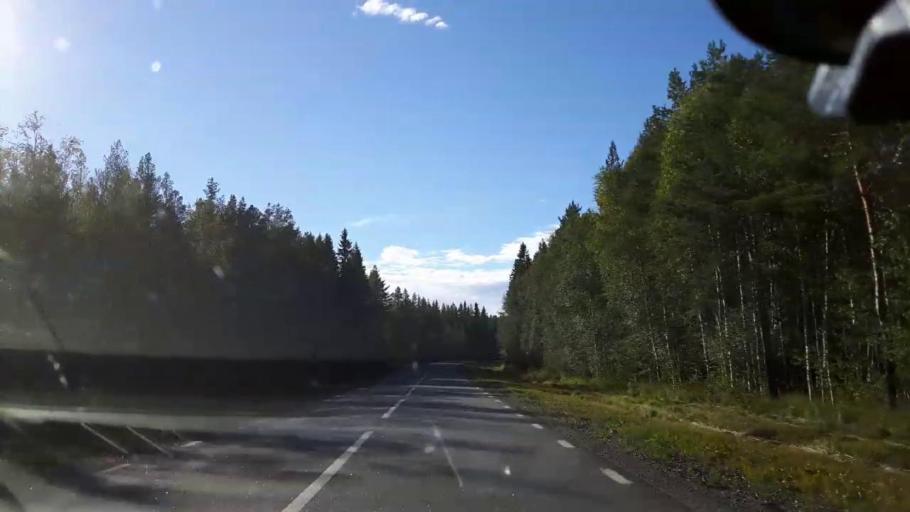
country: SE
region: Jaemtland
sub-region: Ragunda Kommun
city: Hammarstrand
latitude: 63.5336
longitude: 16.0500
